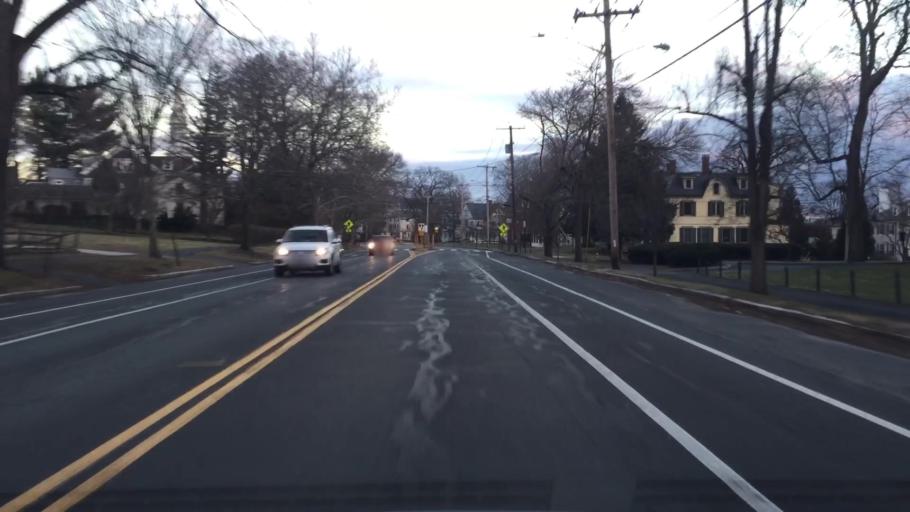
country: US
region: Massachusetts
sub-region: Hampshire County
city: Northampton
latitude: 42.3215
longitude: -72.6428
